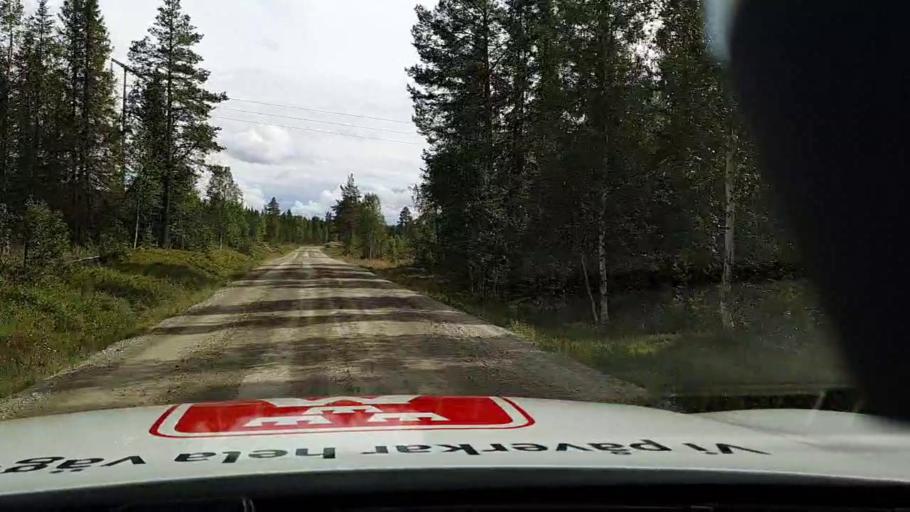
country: SE
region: Jaemtland
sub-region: Are Kommun
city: Jarpen
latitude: 62.5287
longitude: 13.4852
